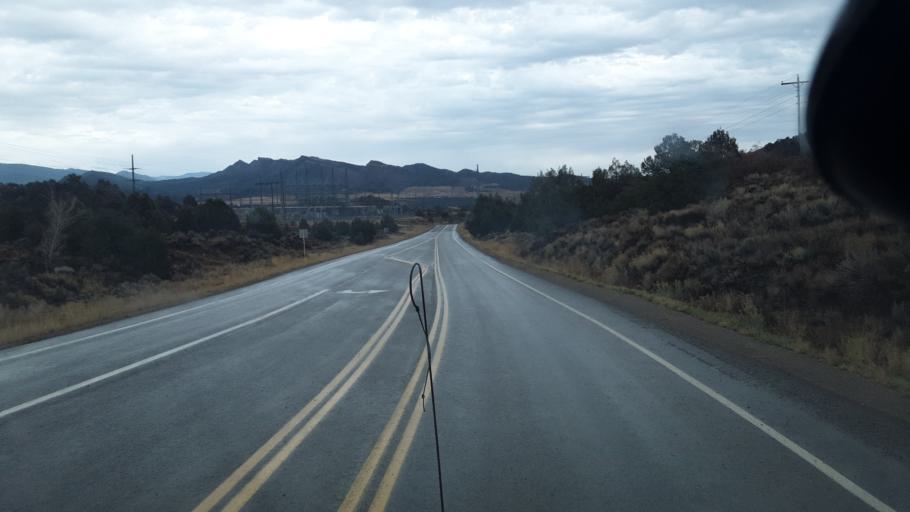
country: US
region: Colorado
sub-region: La Plata County
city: Durango
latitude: 37.2420
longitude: -107.9026
